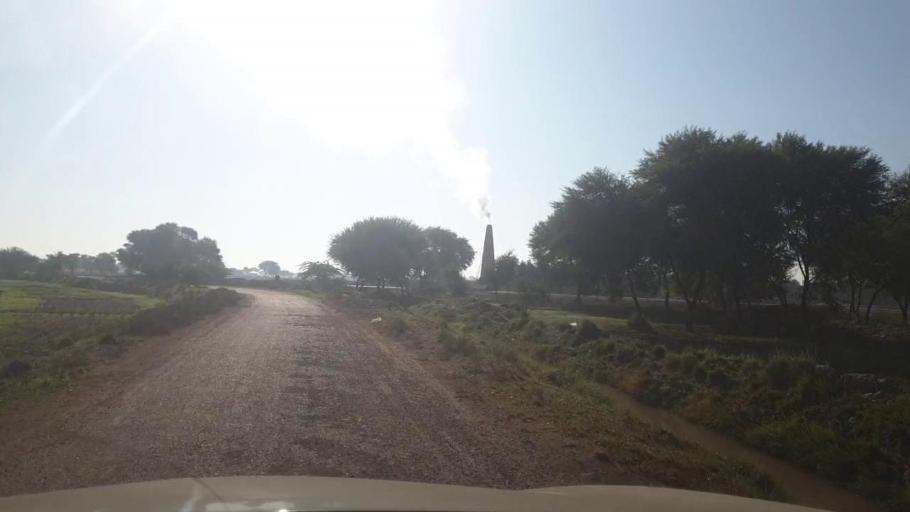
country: PK
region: Sindh
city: Bhan
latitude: 26.5419
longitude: 67.6848
